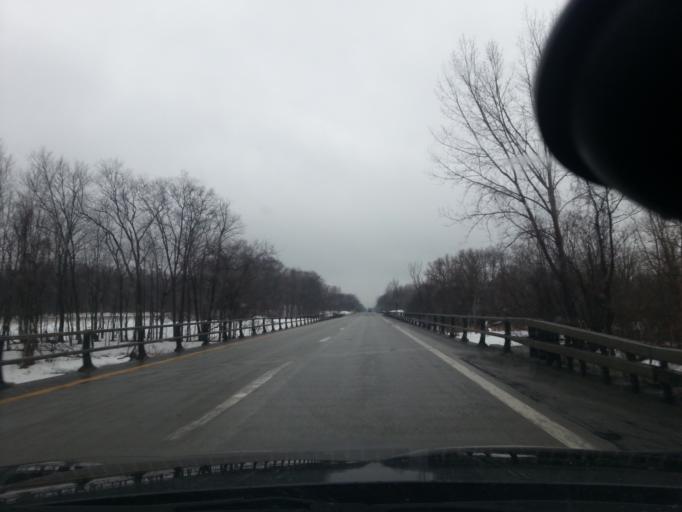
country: US
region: New York
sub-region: Jefferson County
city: Adams
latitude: 43.7752
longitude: -76.0455
